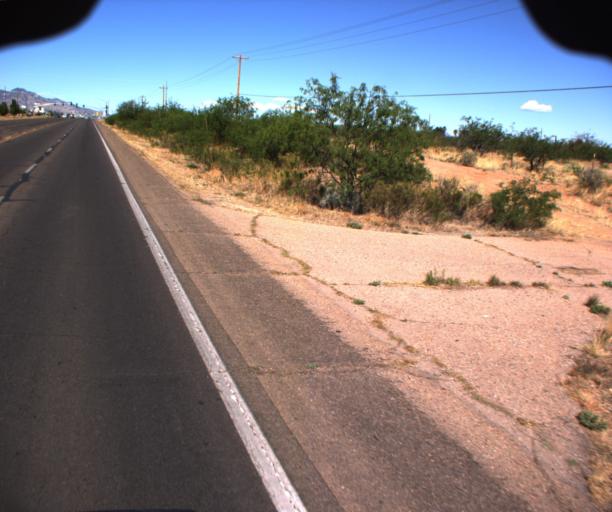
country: US
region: Arizona
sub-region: Cochise County
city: Sierra Vista
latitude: 31.5547
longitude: -110.2372
